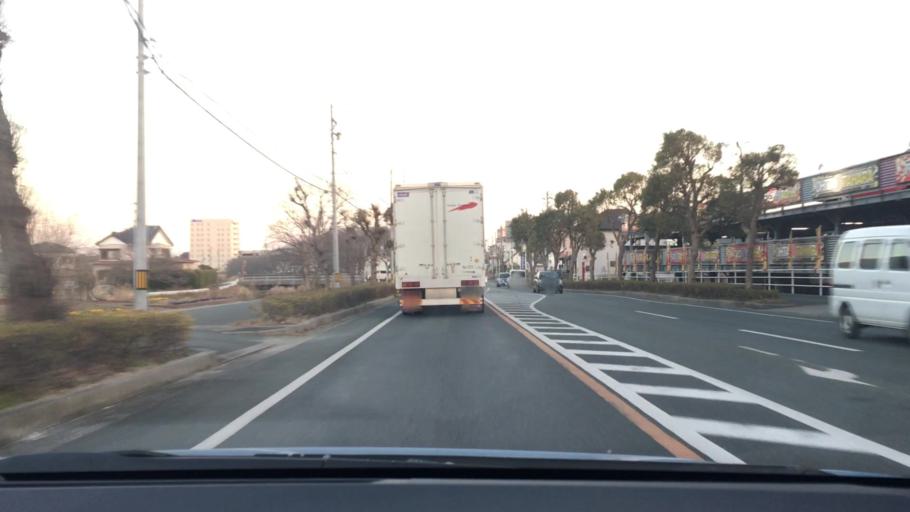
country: JP
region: Aichi
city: Tahara
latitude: 34.6674
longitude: 137.2630
